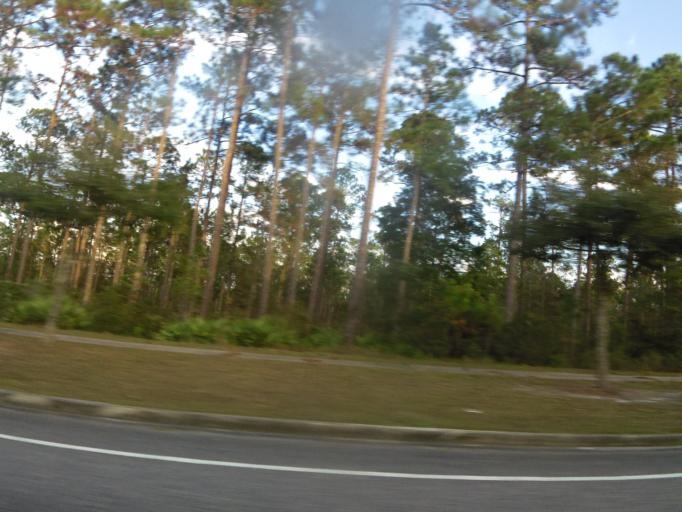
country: US
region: Florida
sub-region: Duval County
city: Baldwin
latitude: 30.2561
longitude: -81.8864
